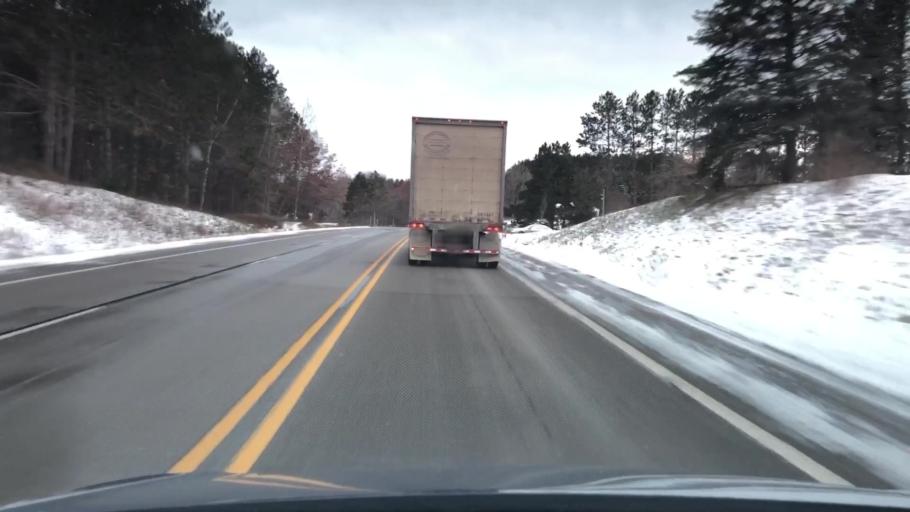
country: US
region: Michigan
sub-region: Wexford County
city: Cadillac
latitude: 44.1812
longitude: -85.3826
